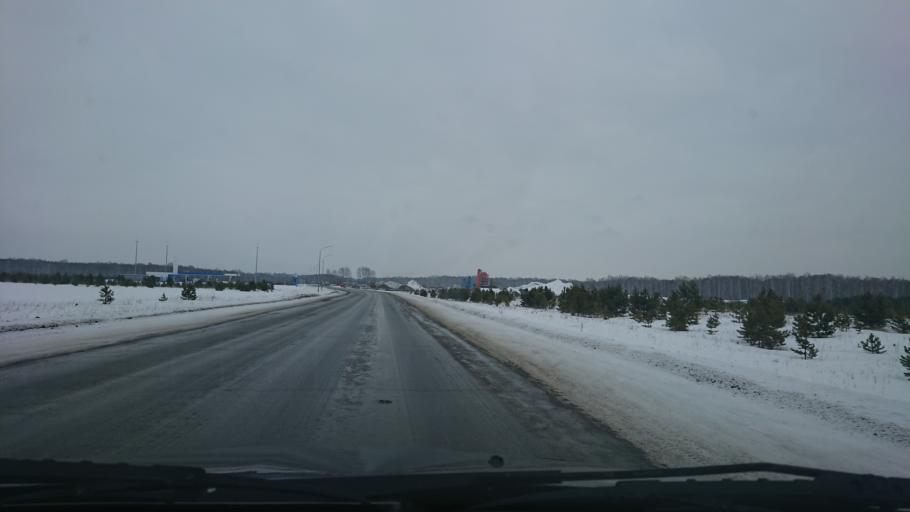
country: RU
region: Chelyabinsk
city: Tyubuk
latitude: 56.0502
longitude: 60.9799
